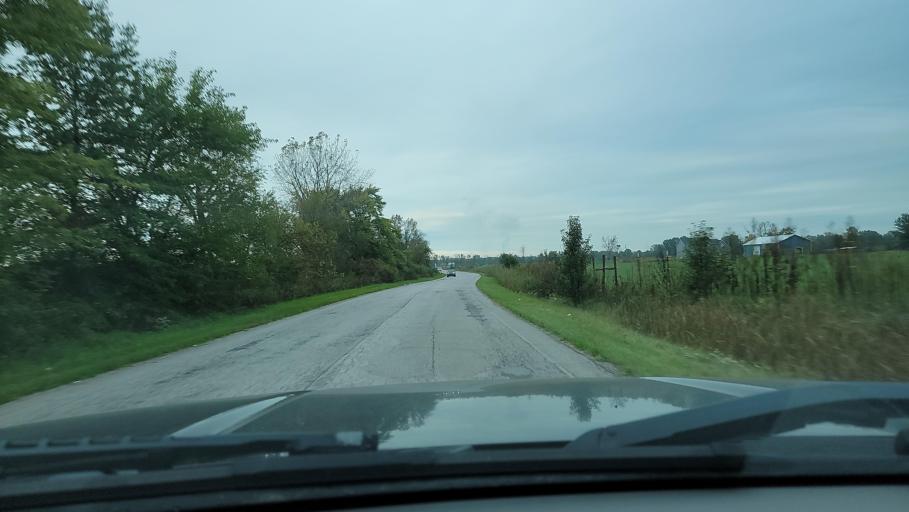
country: US
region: Indiana
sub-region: Porter County
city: South Haven
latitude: 41.5581
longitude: -87.1532
